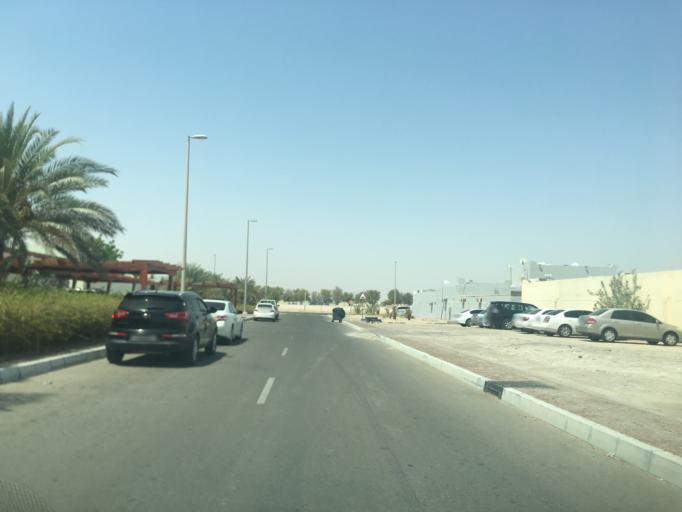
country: AE
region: Abu Dhabi
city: Abu Dhabi
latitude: 24.3085
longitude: 54.6353
